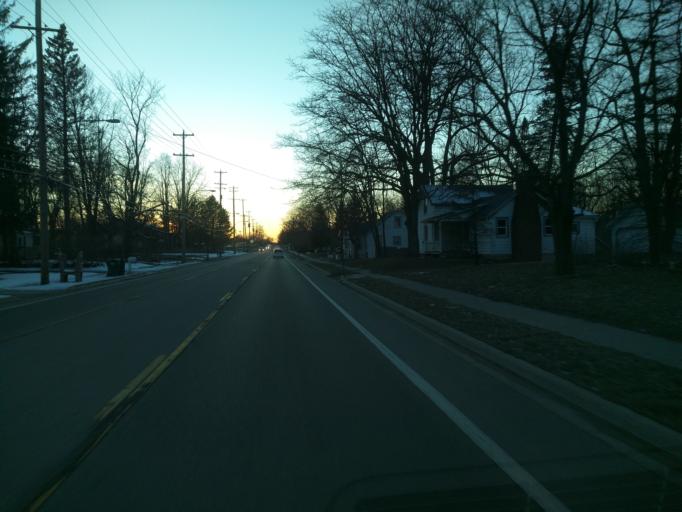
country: US
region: Michigan
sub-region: Ingham County
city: Lansing
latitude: 42.6976
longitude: -84.5769
